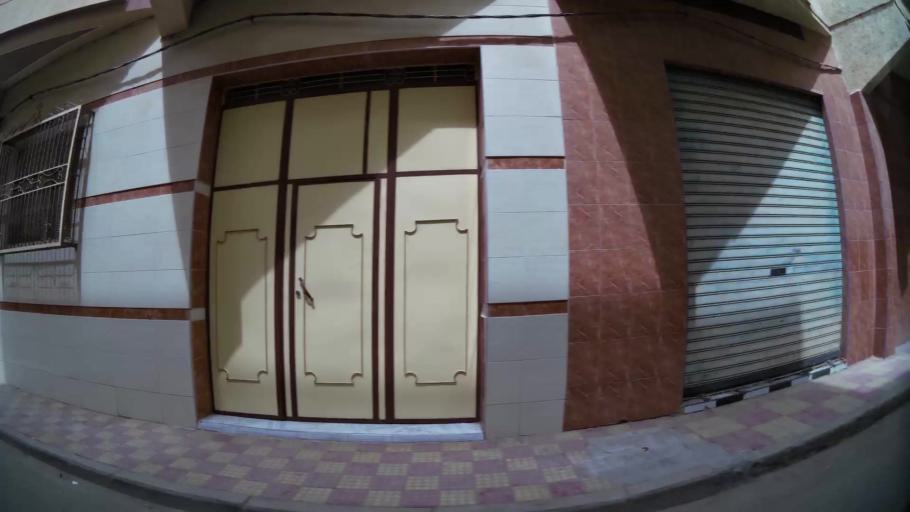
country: MA
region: Oriental
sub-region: Nador
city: Nador
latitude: 35.1664
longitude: -2.9270
